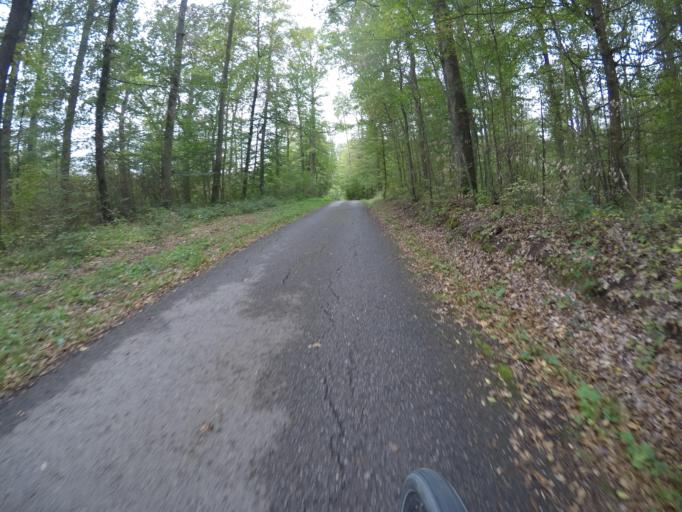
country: DE
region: Baden-Wuerttemberg
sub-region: Karlsruhe Region
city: Sternenfels
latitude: 48.9994
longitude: 8.8581
